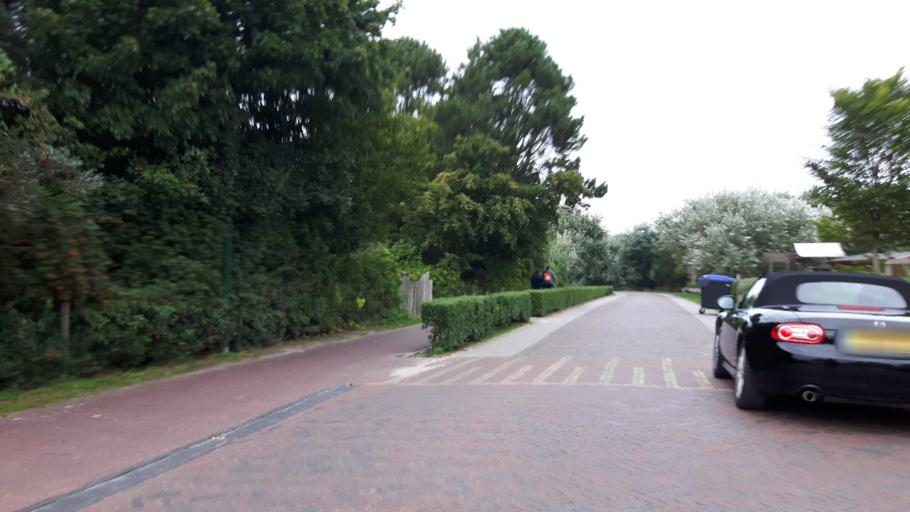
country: NL
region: Friesland
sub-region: Gemeente Ameland
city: Nes
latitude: 53.4524
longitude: 5.7760
